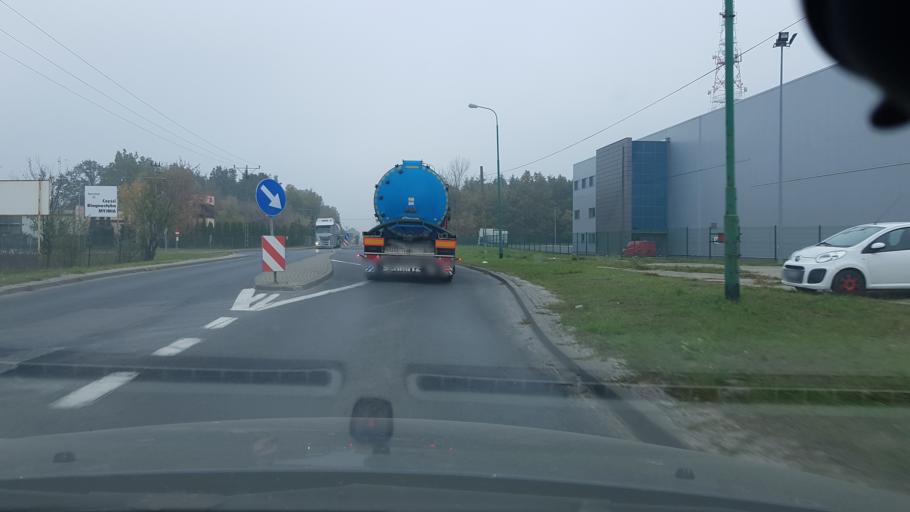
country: PL
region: Lodz Voivodeship
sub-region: Powiat tomaszowski
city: Tomaszow Mazowiecki
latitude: 51.5585
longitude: 20.0199
